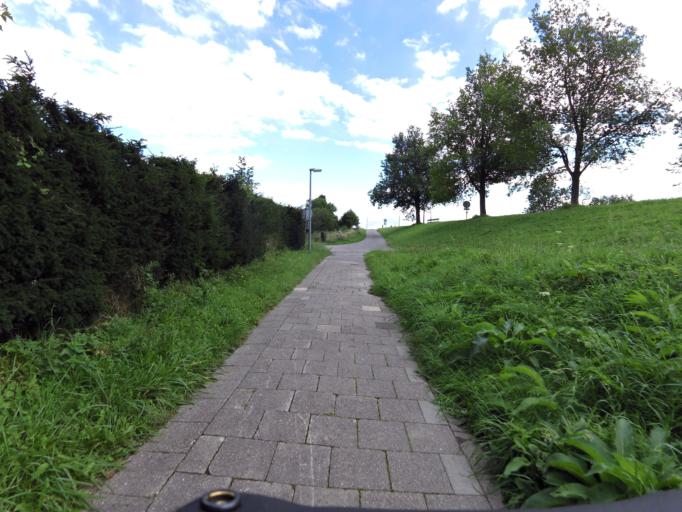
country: NL
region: North Brabant
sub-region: Gemeente Steenbergen
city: Dinteloord
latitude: 51.6917
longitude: 4.2704
